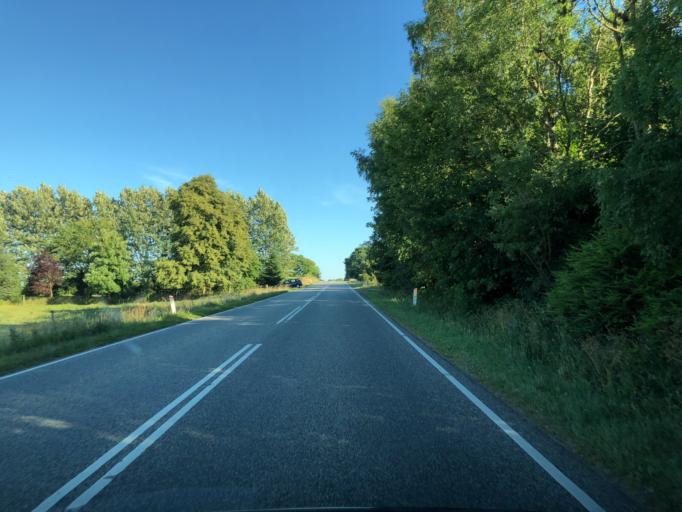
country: DK
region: Central Jutland
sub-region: Skanderborg Kommune
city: Stilling
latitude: 56.0814
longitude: 9.9726
